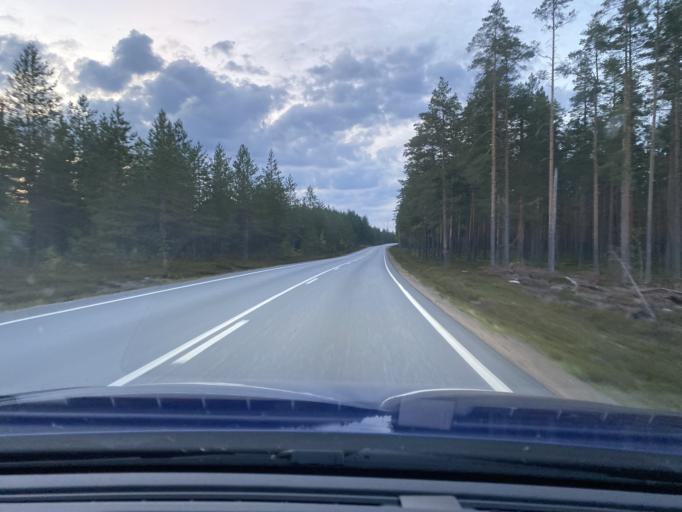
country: FI
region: Southern Ostrobothnia
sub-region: Suupohja
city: Kauhajoki
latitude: 62.2301
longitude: 22.2715
